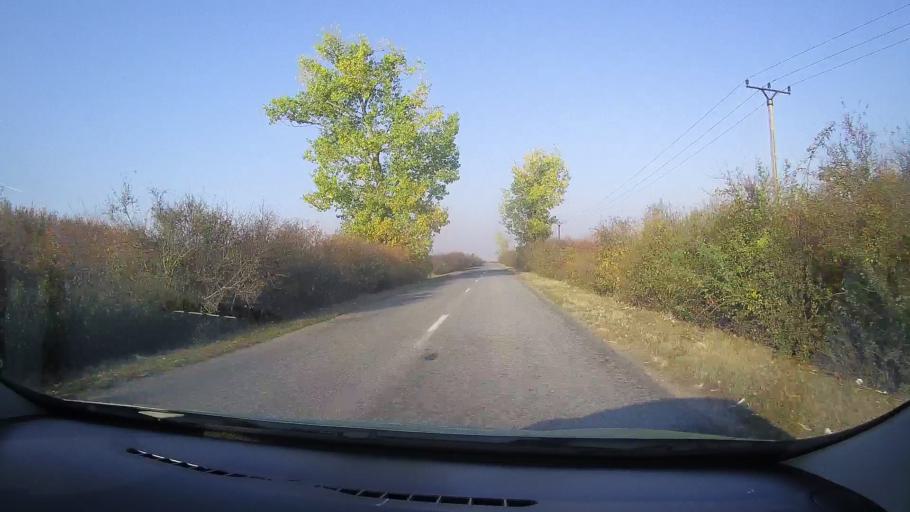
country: RO
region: Arad
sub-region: Comuna Socodor
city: Socodor
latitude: 46.5033
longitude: 21.4135
